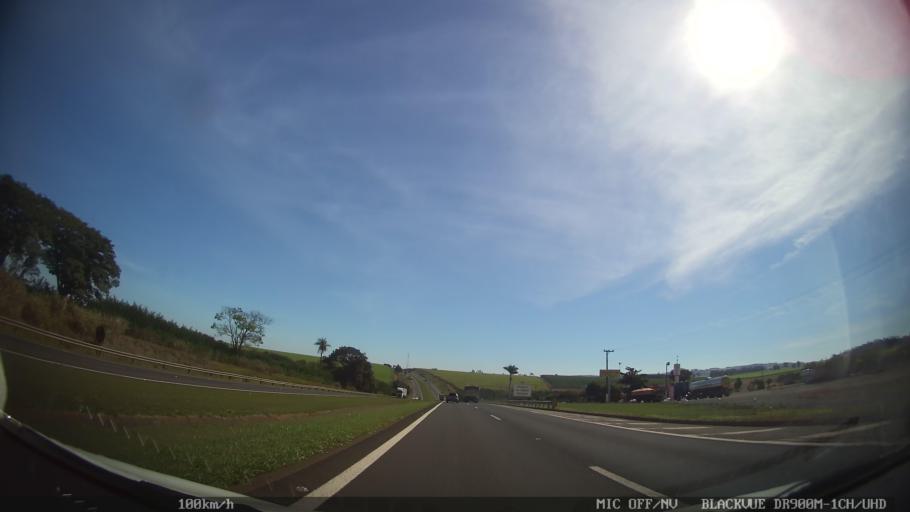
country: BR
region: Sao Paulo
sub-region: Porto Ferreira
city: Porto Ferreira
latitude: -21.8063
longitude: -47.5022
